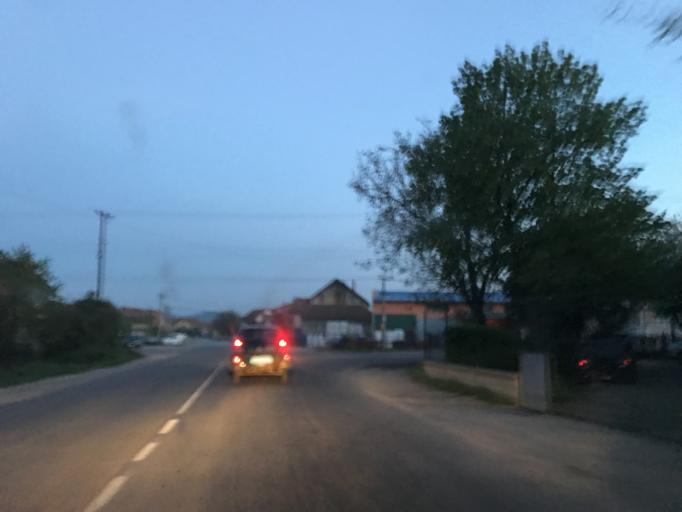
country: RS
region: Central Serbia
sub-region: Zajecarski Okrug
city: Zajecar
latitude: 43.9128
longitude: 22.2957
